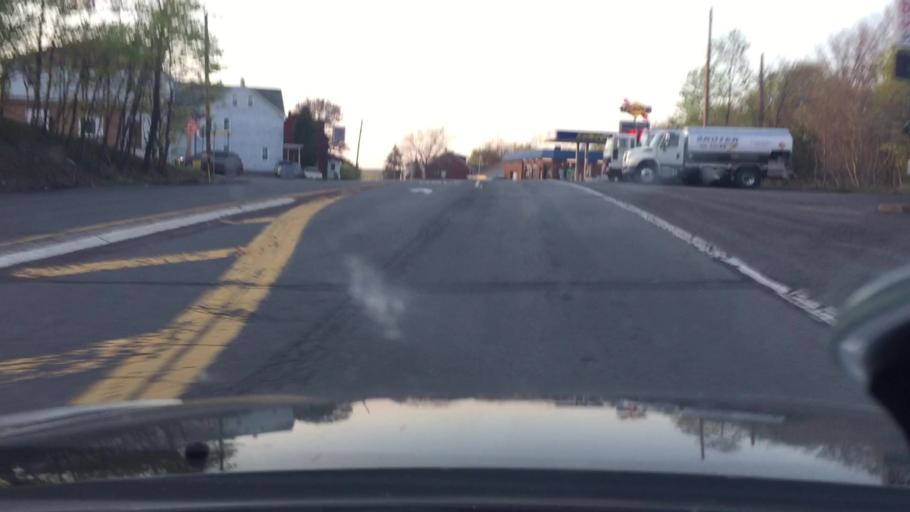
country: US
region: Pennsylvania
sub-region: Schuylkill County
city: McAdoo
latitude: 40.8929
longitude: -75.9955
